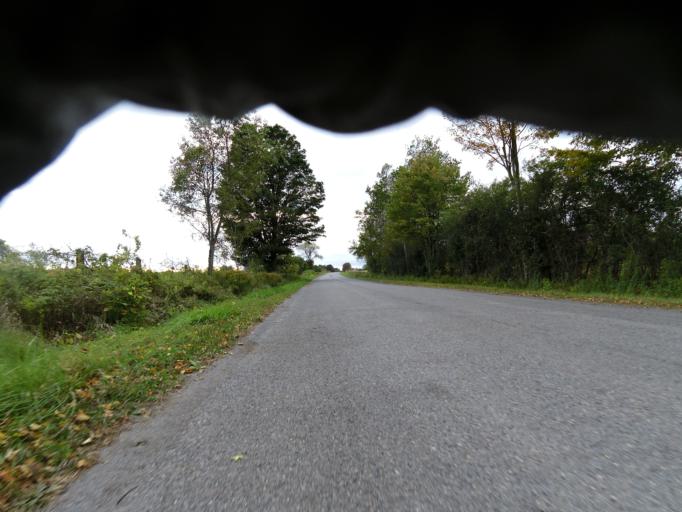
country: CA
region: Ontario
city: Cobourg
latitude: 43.9789
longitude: -77.9292
